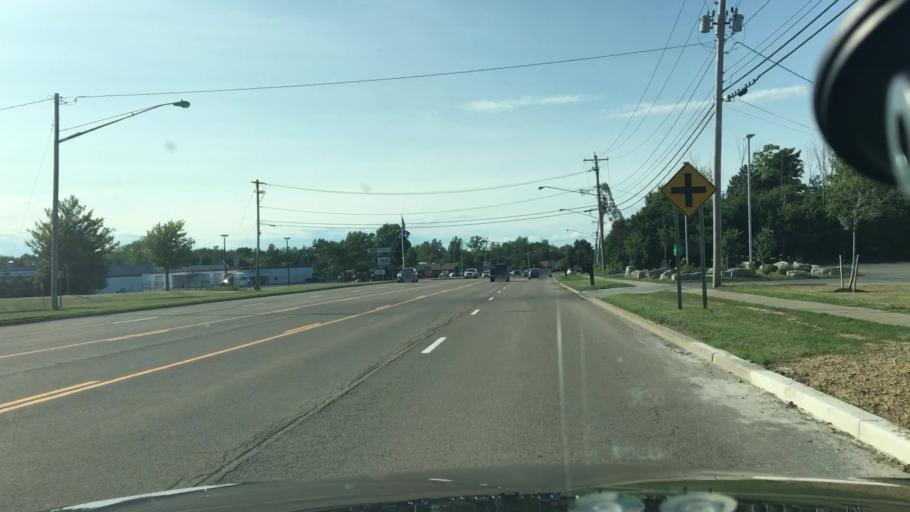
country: US
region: New York
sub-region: Erie County
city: Wanakah
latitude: 42.7562
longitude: -78.8594
